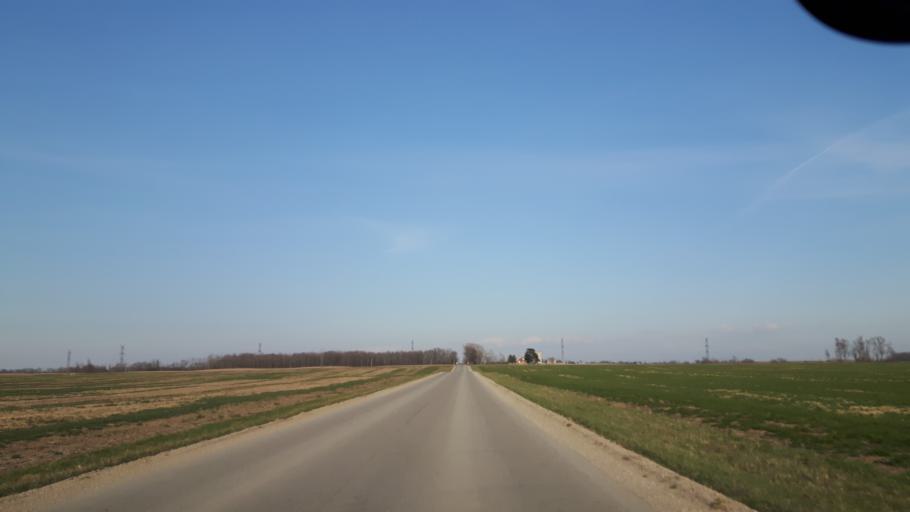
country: CA
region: Ontario
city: Goderich
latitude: 43.6986
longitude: -81.6735
